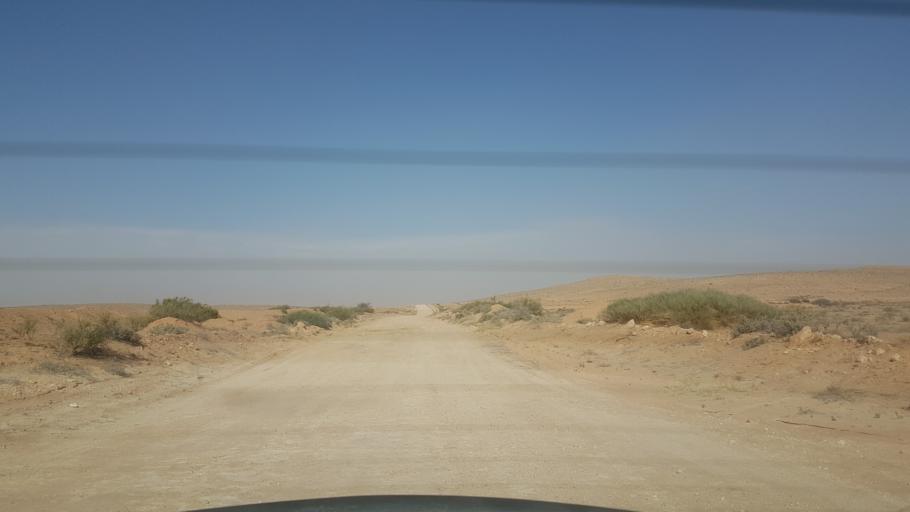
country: TN
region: Qabis
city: El Hamma
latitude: 33.6522
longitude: 9.7363
